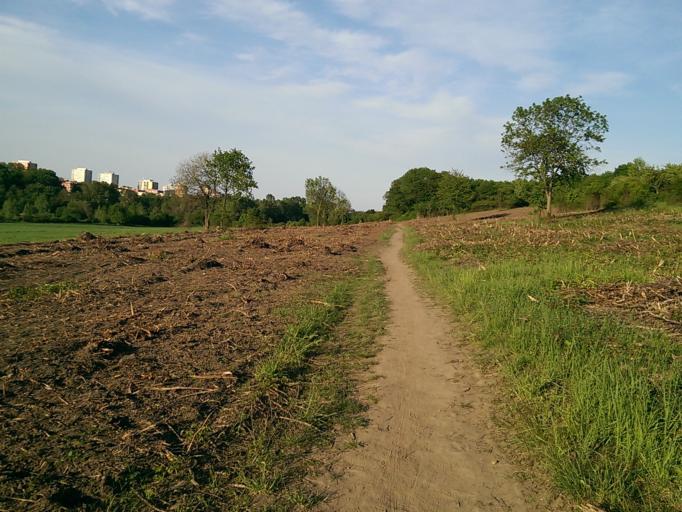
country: CZ
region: Praha
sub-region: Praha 9
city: Vysocany
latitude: 50.0475
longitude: 14.5031
